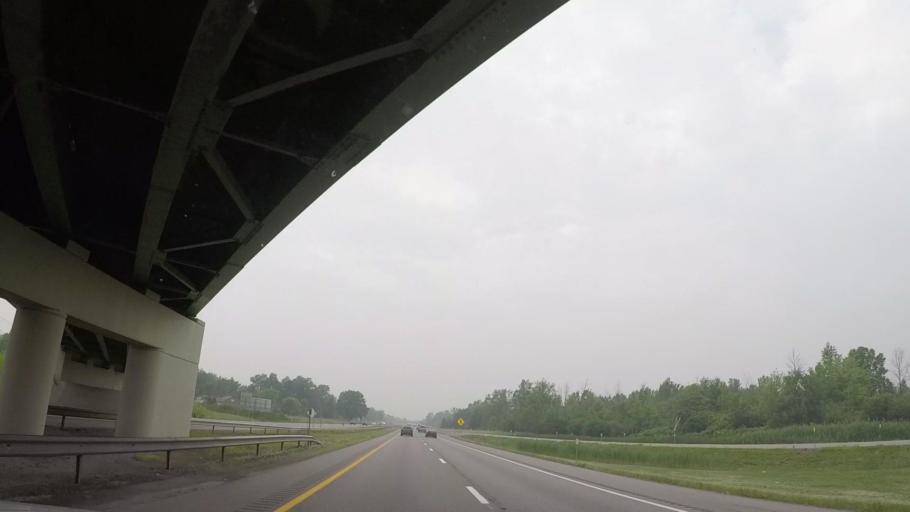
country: US
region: New York
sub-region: Erie County
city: Grandyle Village
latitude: 43.0072
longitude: -78.9533
